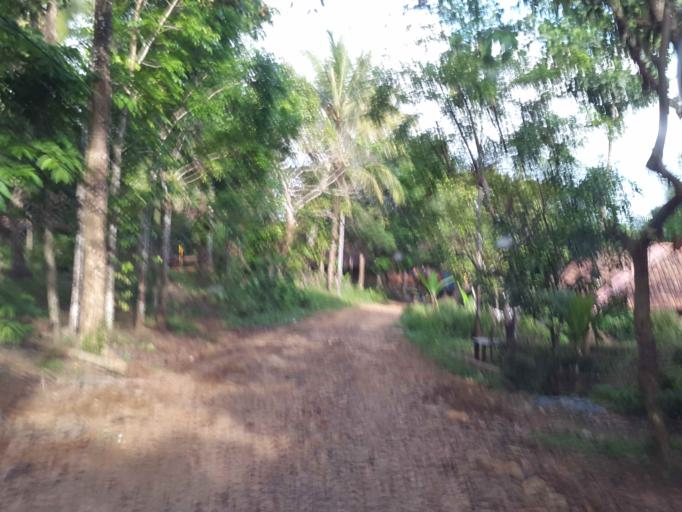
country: ID
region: Banten
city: Cibaliung
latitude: -6.7058
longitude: 105.7211
